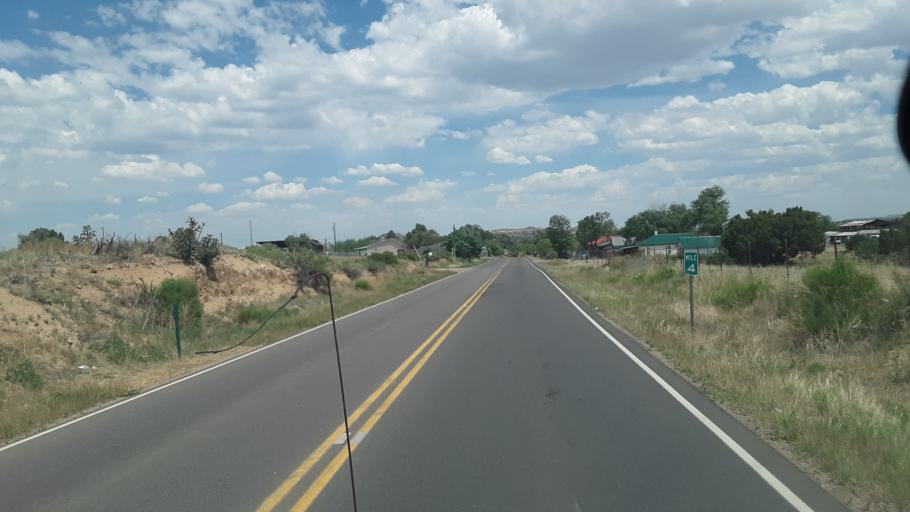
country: US
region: Colorado
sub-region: Fremont County
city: Lincoln Park
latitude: 38.4176
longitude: -105.1880
